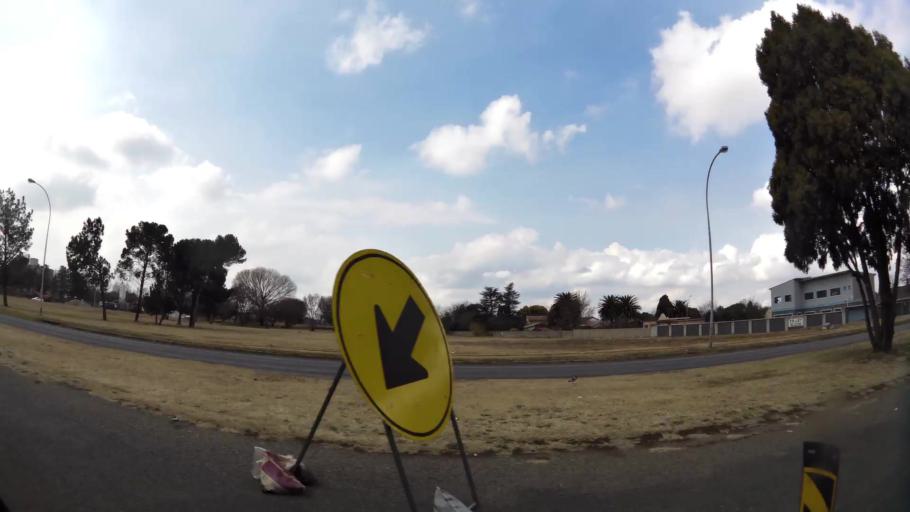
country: ZA
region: Gauteng
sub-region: Sedibeng District Municipality
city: Vanderbijlpark
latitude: -26.7074
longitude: 27.8359
